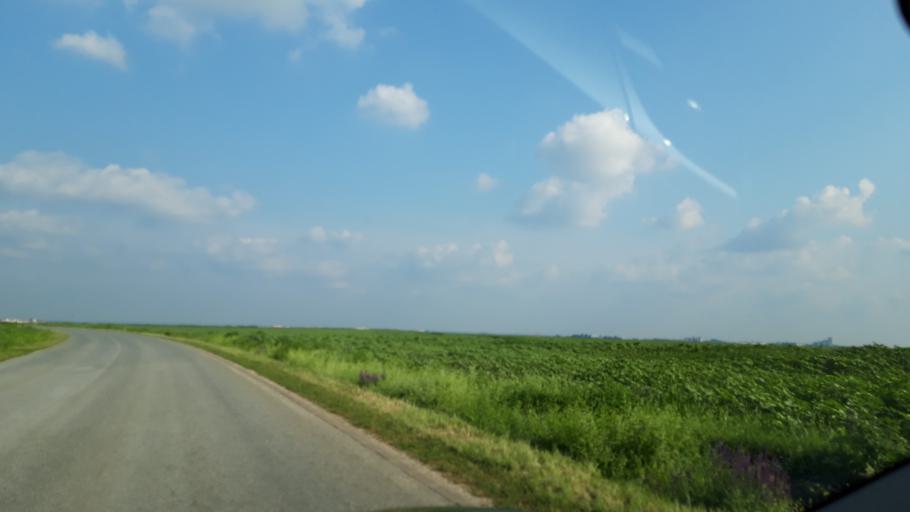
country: RS
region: Autonomna Pokrajina Vojvodina
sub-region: Sremski Okrug
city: Ingija
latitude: 45.0900
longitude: 20.0986
